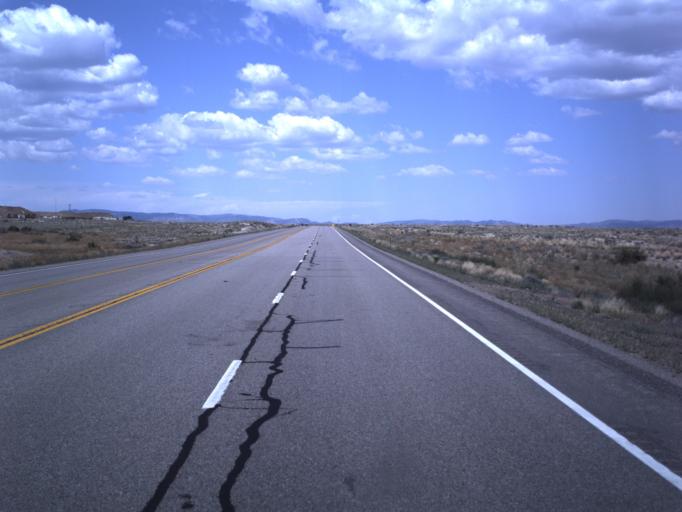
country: US
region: Utah
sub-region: Carbon County
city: Price
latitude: 39.5267
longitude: -110.8218
